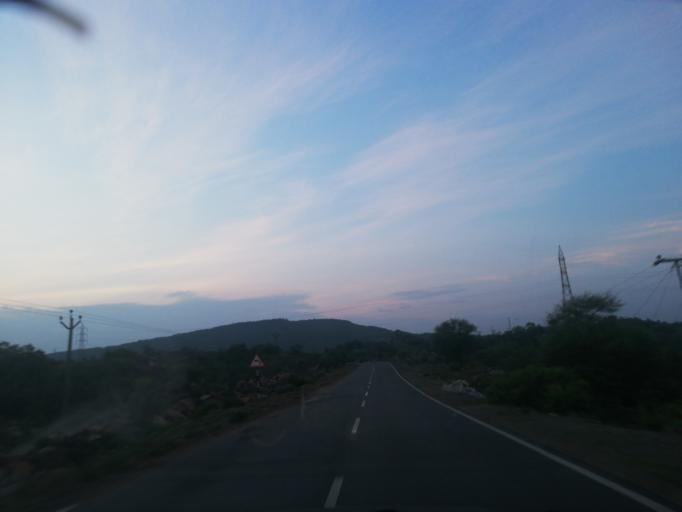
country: IN
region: Andhra Pradesh
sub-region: Guntur
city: Macherla
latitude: 16.6679
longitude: 79.2818
